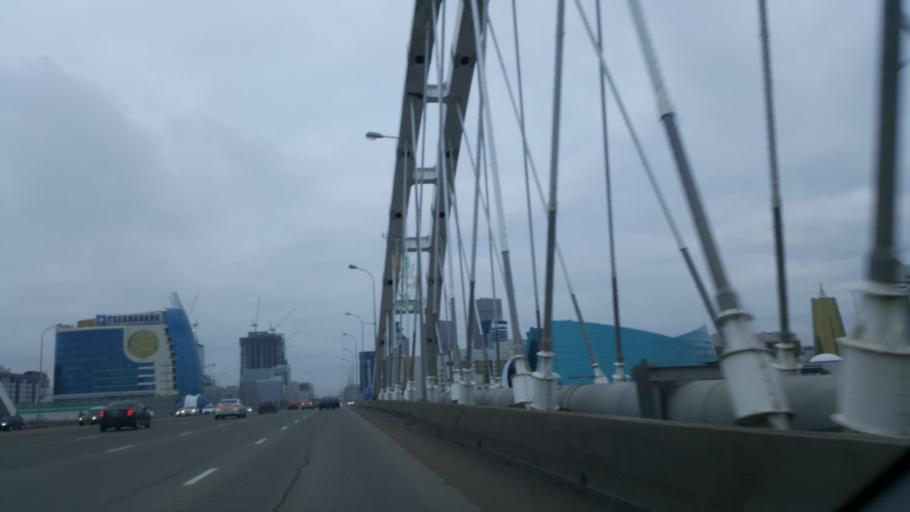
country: KZ
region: Astana Qalasy
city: Astana
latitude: 51.1207
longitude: 71.4461
